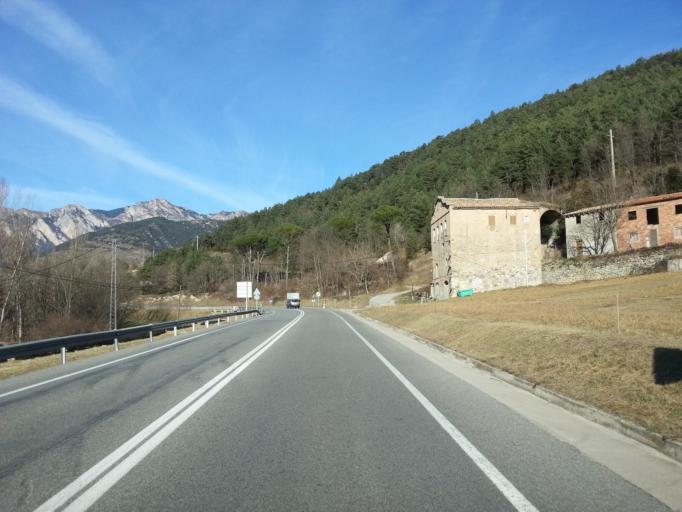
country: ES
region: Catalonia
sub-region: Provincia de Barcelona
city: Guardiola de Bergueda
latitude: 42.2403
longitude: 1.8738
